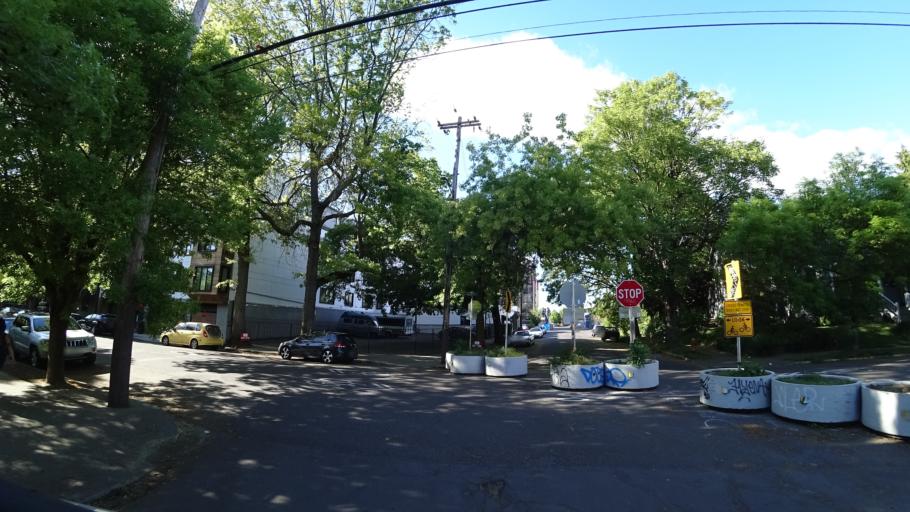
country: US
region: Oregon
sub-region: Multnomah County
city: Portland
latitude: 45.5221
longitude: -122.6507
